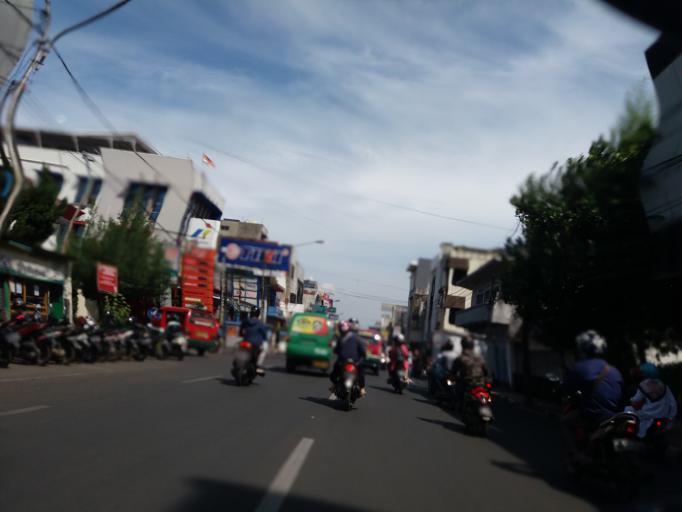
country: ID
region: West Java
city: Bandung
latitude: -6.9299
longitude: 107.6035
